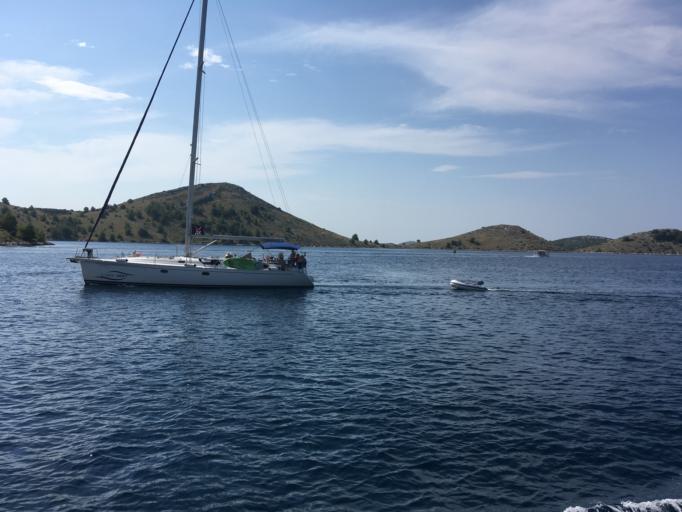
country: HR
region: Zadarska
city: Sali
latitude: 43.8876
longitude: 15.2117
